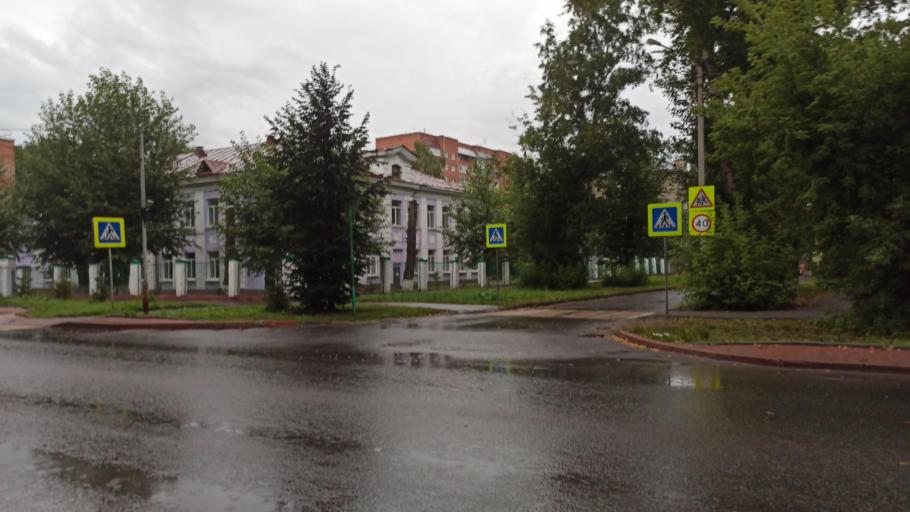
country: RU
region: Tomsk
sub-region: Tomskiy Rayon
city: Tomsk
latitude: 56.4638
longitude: 84.9728
